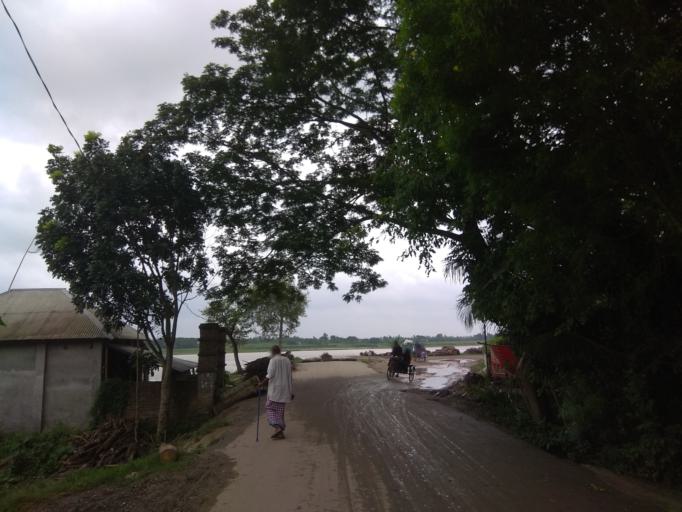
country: BD
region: Dhaka
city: Dohar
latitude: 23.4185
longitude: 90.0706
